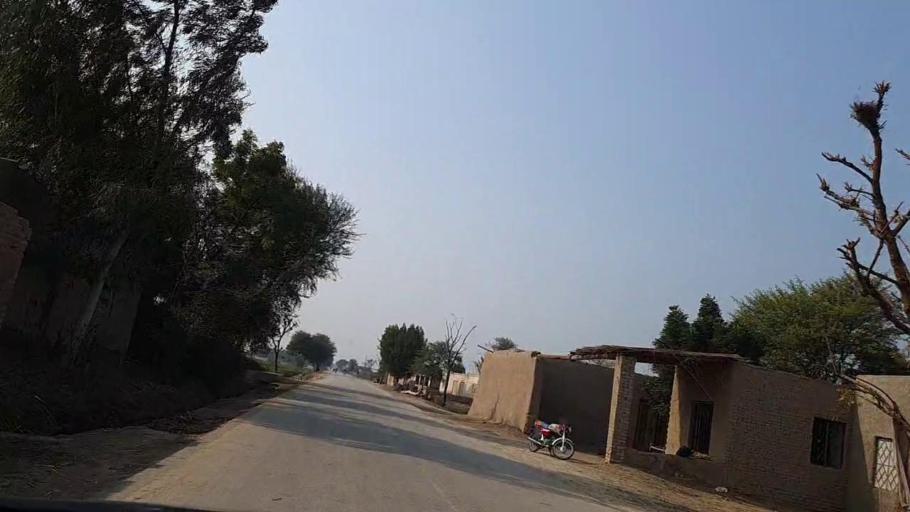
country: PK
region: Sindh
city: Sann
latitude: 26.1427
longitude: 68.1514
